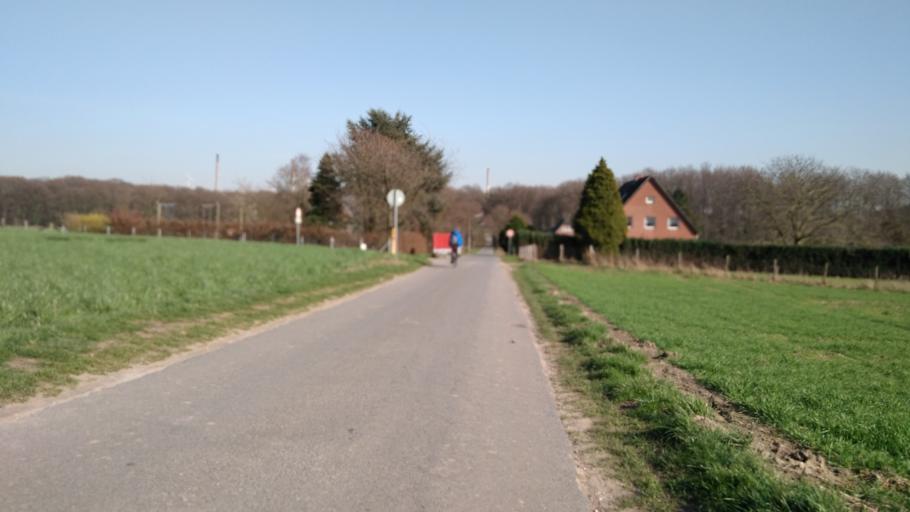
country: DE
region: North Rhine-Westphalia
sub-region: Regierungsbezirk Munster
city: Gladbeck
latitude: 51.5974
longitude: 6.9506
